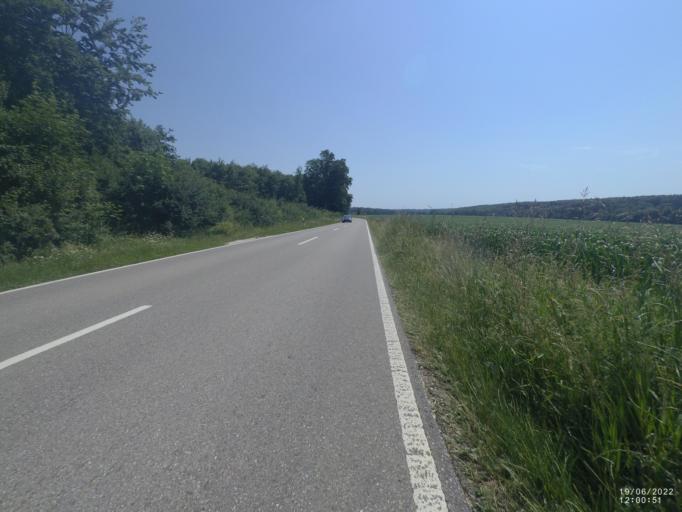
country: DE
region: Baden-Wuerttemberg
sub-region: Tuebingen Region
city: Weidenstetten
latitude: 48.6018
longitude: 9.9655
